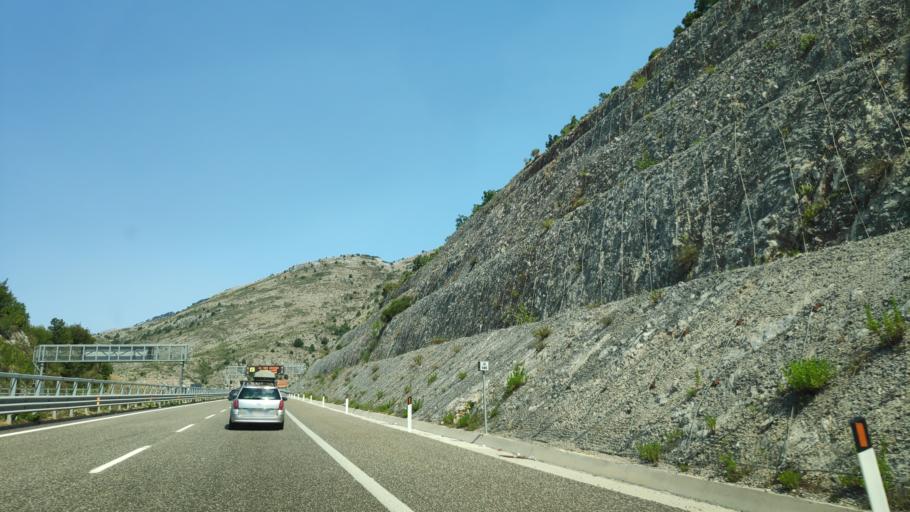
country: IT
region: Basilicate
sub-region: Provincia di Potenza
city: Lauria
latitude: 40.0312
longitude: 15.8748
